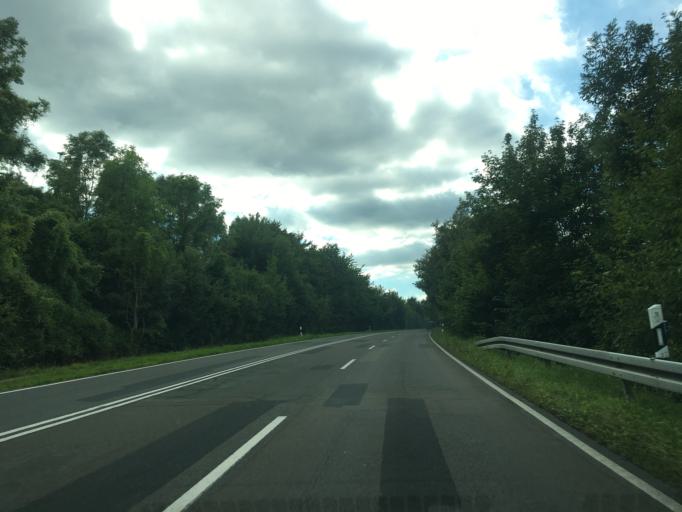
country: DE
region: North Rhine-Westphalia
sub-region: Regierungsbezirk Detmold
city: Lugde
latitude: 51.9768
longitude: 9.2032
